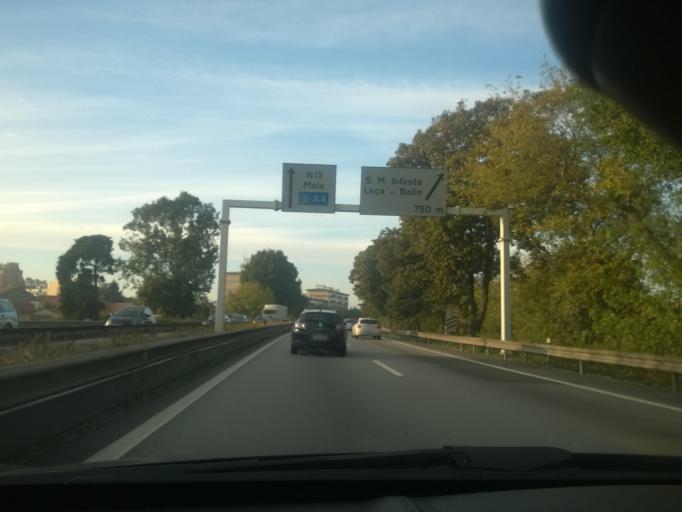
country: PT
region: Porto
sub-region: Matosinhos
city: Senhora da Hora
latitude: 41.1907
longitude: -8.6275
